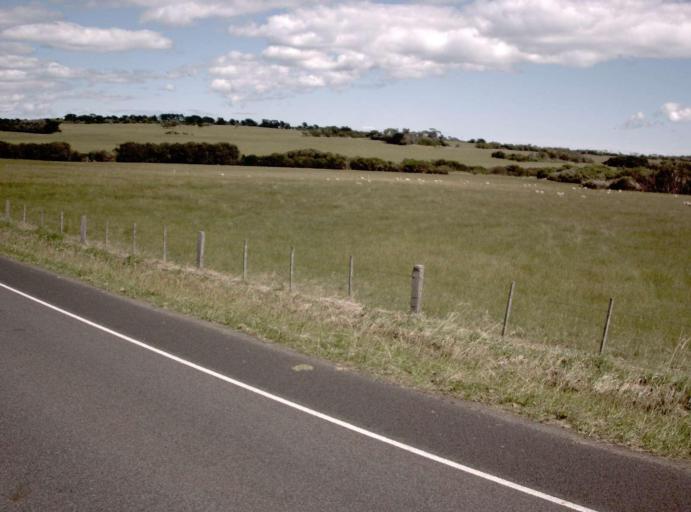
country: AU
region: Victoria
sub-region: Bass Coast
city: Phillip Island
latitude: -38.4966
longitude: 145.1801
